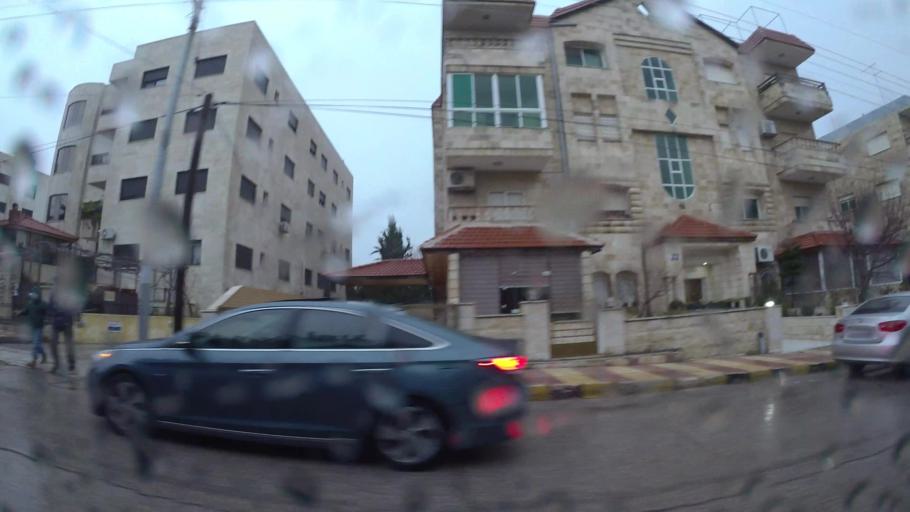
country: JO
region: Amman
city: Al Jubayhah
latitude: 32.0282
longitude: 35.8533
